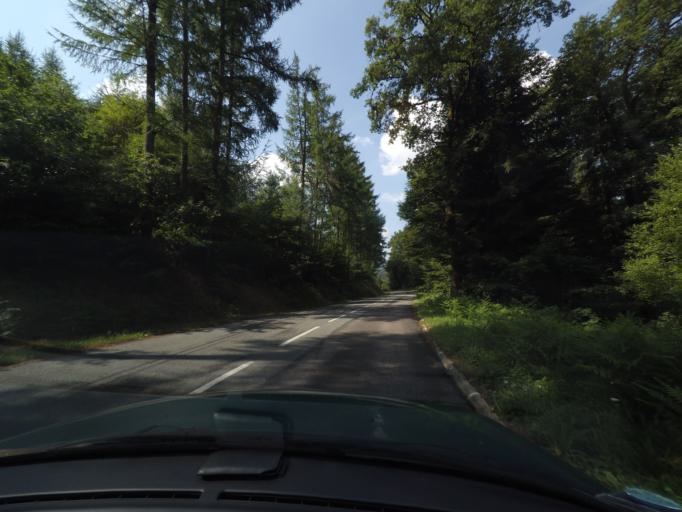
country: FR
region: Limousin
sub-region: Departement de la Haute-Vienne
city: Eymoutiers
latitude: 45.7183
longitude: 1.8599
